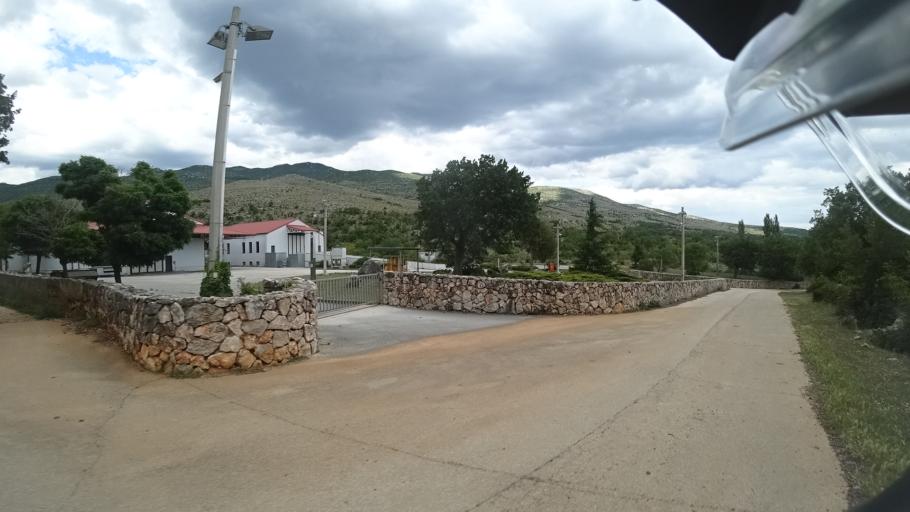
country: HR
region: Zadarska
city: Gracac
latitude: 44.1940
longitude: 15.9080
